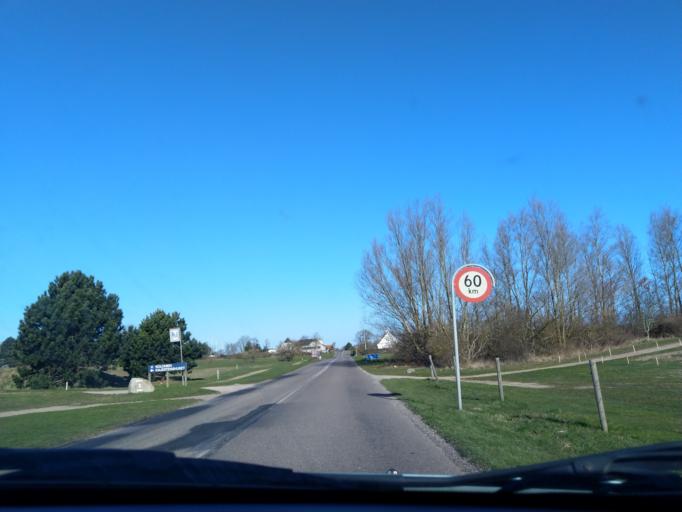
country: DK
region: Zealand
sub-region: Kalundborg Kommune
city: Kalundborg
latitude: 55.7209
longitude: 11.0087
